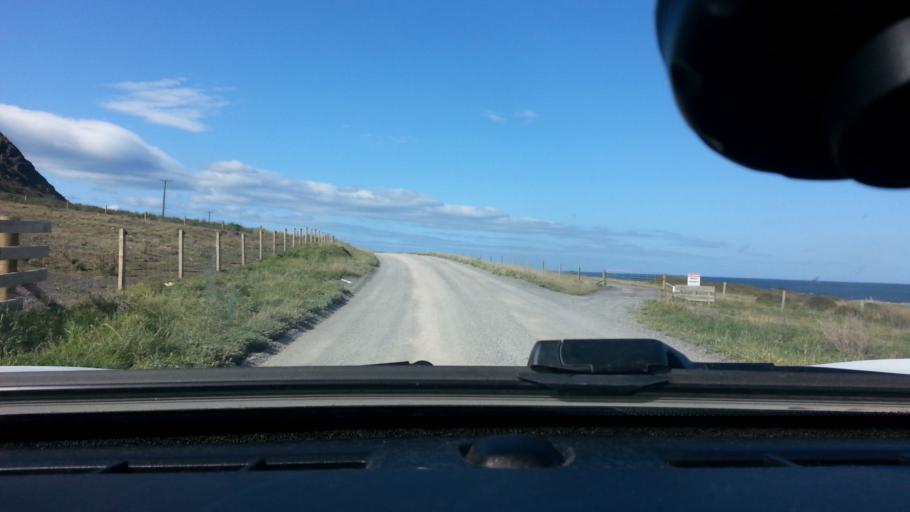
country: NZ
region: Wellington
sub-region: South Wairarapa District
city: Waipawa
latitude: -41.5911
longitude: 175.2332
